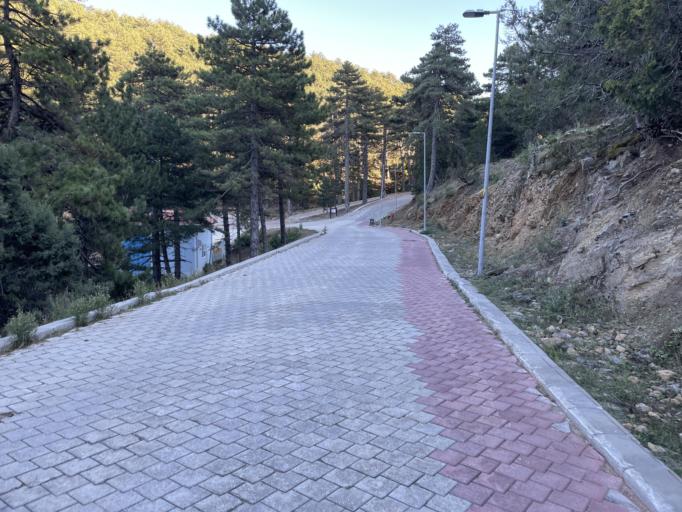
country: TR
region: Denizli
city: Denizli
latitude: 37.7017
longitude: 29.1410
